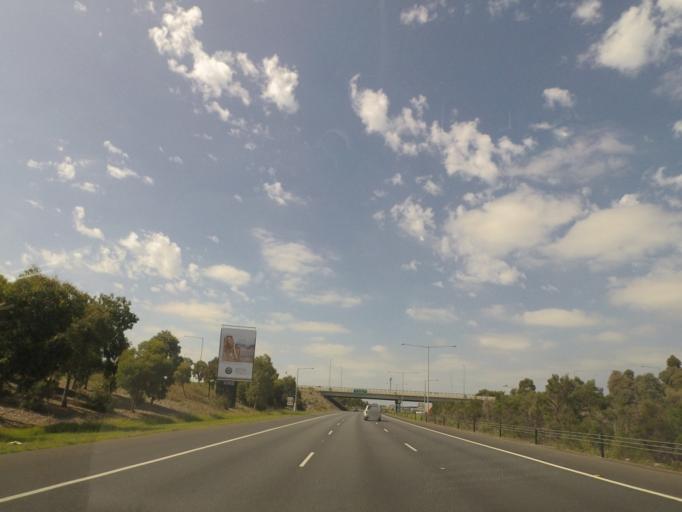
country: AU
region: Victoria
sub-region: Greater Dandenong
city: Dandenong
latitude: -37.9995
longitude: 145.1918
